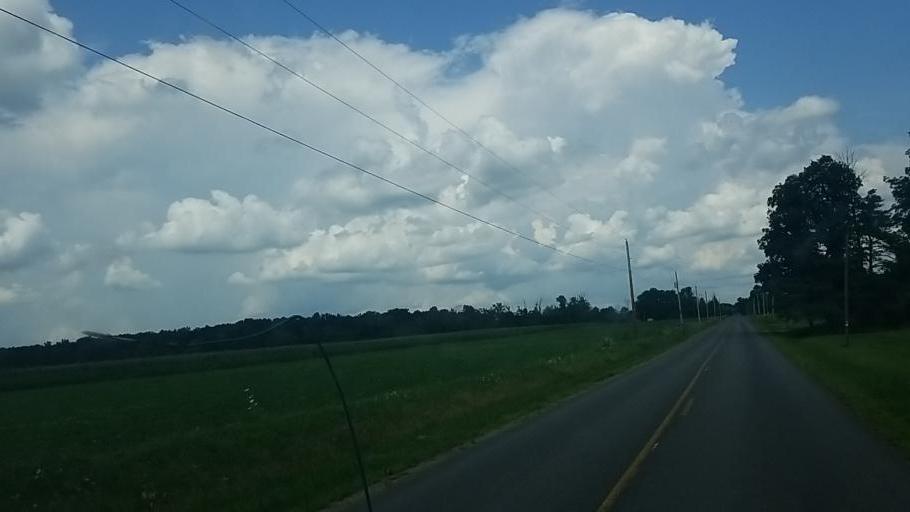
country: US
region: Ohio
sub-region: Medina County
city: Lodi
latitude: 41.0695
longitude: -82.0764
